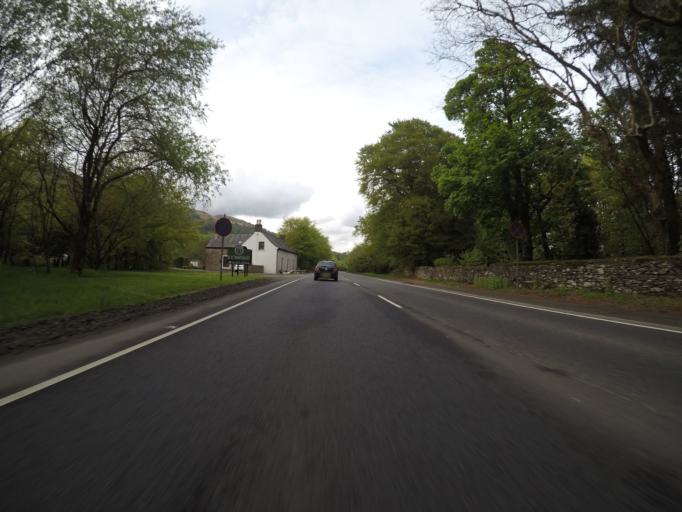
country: GB
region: Scotland
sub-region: West Dunbartonshire
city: Balloch
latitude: 56.0629
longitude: -4.6460
